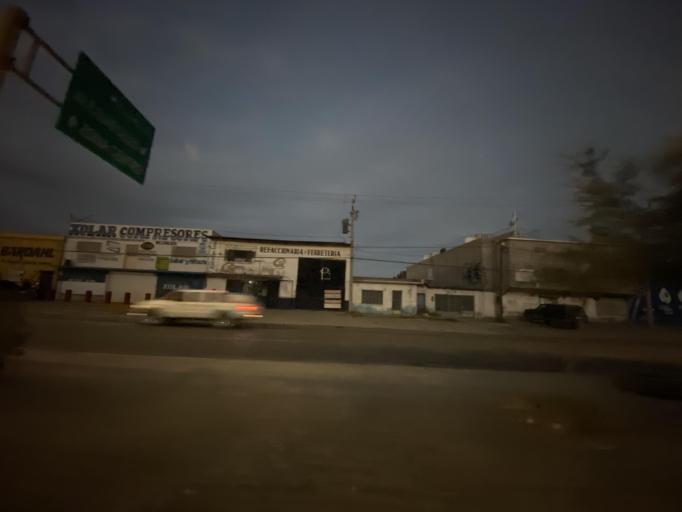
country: MX
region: Chihuahua
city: Ciudad Juarez
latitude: 31.7048
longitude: -106.4464
